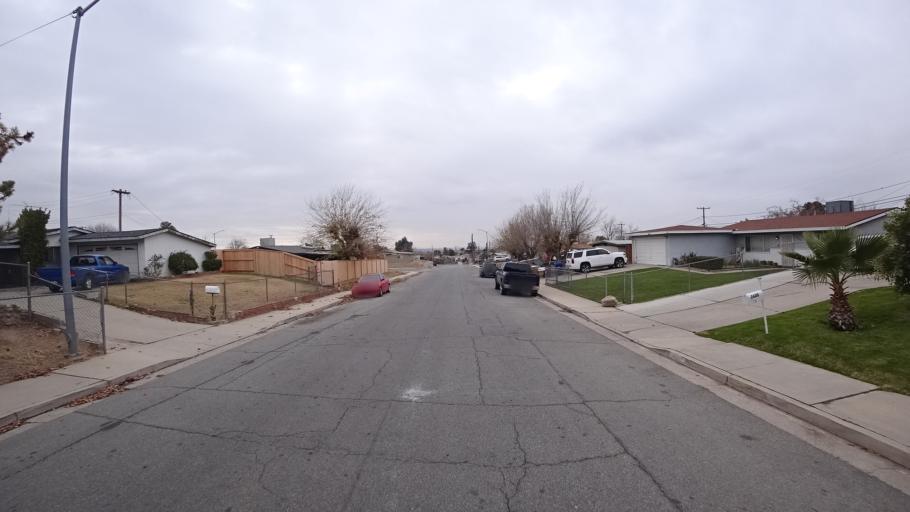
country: US
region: California
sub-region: Kern County
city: Bakersfield
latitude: 35.3818
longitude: -118.9284
